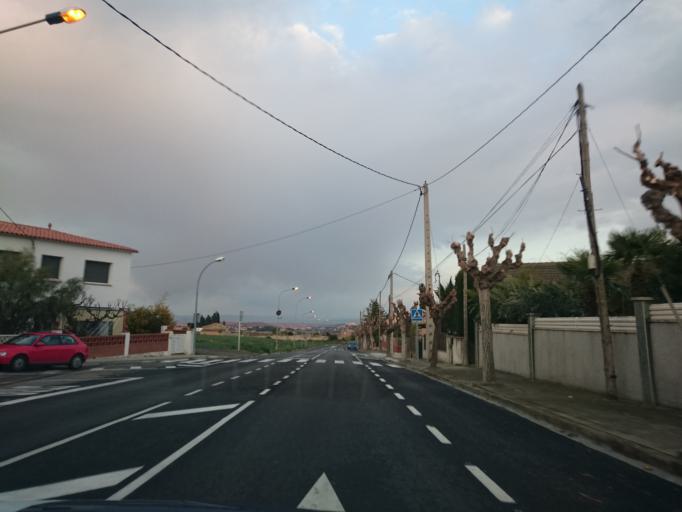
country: ES
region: Catalonia
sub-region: Provincia de Barcelona
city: Sant Marti Sarroca
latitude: 41.3900
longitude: 1.5670
